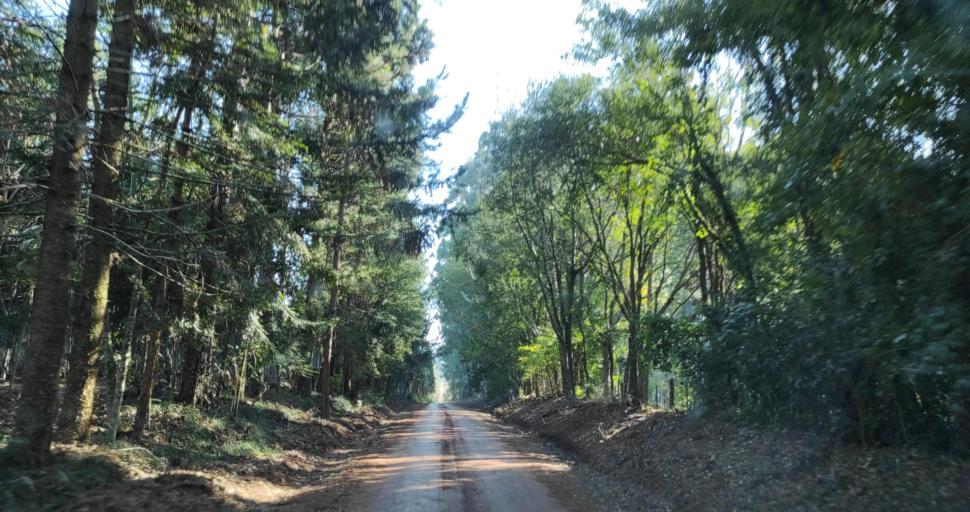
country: AR
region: Misiones
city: Capiovi
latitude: -26.8765
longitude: -55.0163
